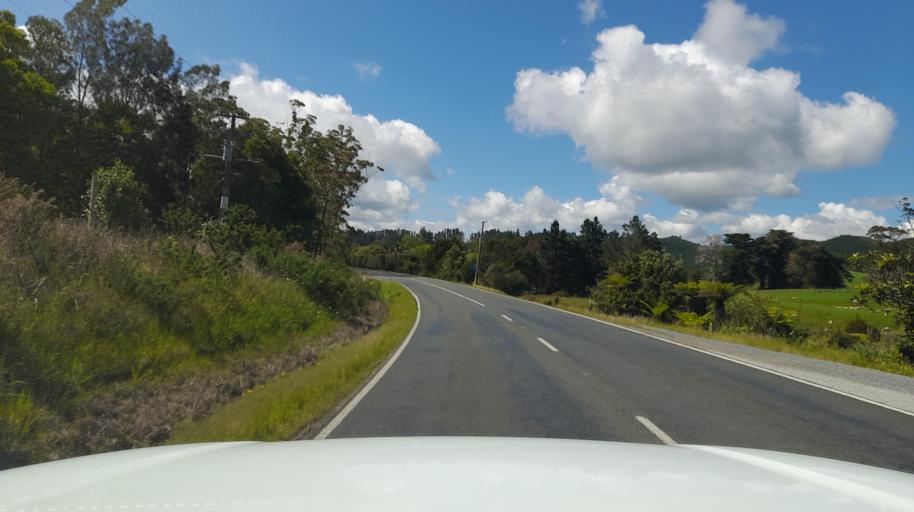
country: NZ
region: Northland
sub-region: Far North District
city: Taipa
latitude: -35.0247
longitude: 173.4760
